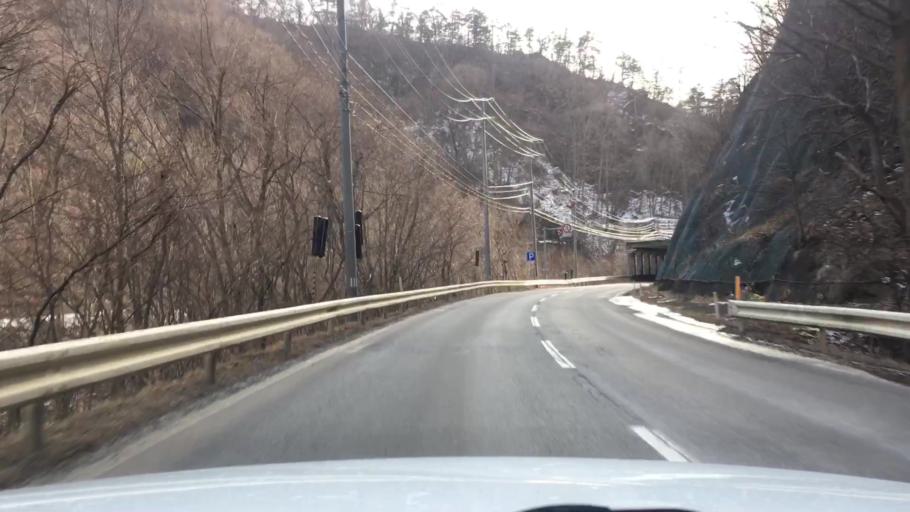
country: JP
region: Iwate
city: Tono
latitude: 39.6359
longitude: 141.5369
